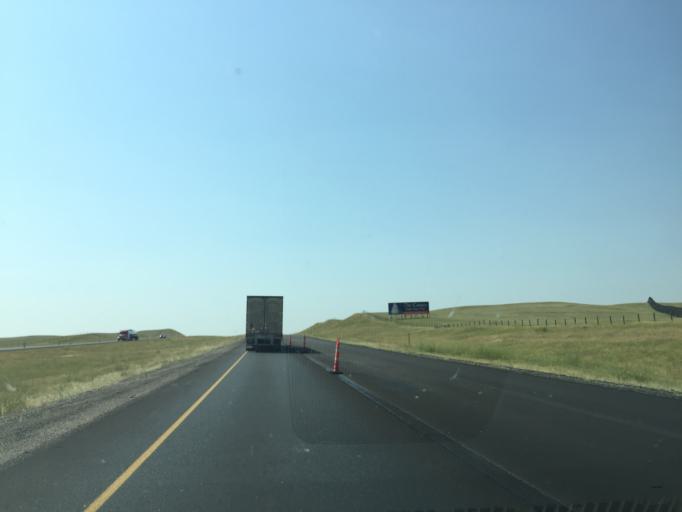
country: US
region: Wyoming
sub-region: Laramie County
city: Ranchettes
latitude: 41.3222
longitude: -104.8614
